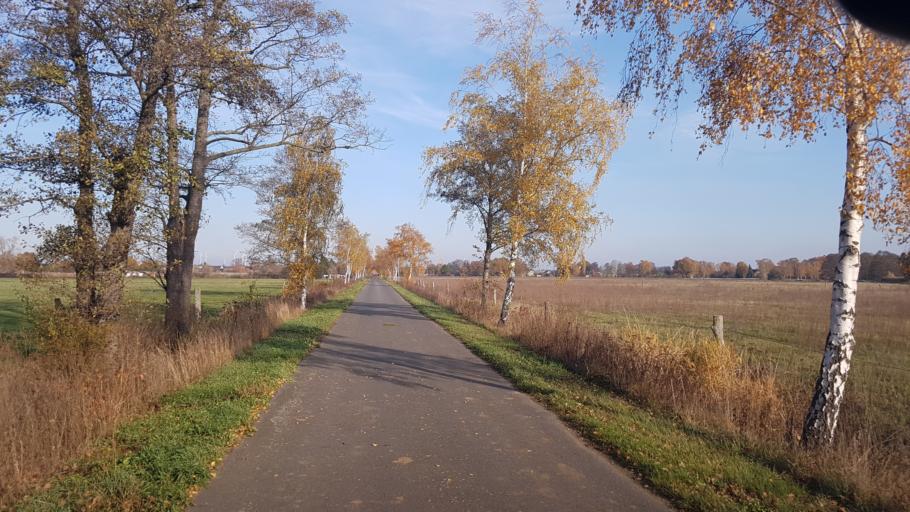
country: DE
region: Brandenburg
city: Falkenberg
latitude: 51.6235
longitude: 13.3089
